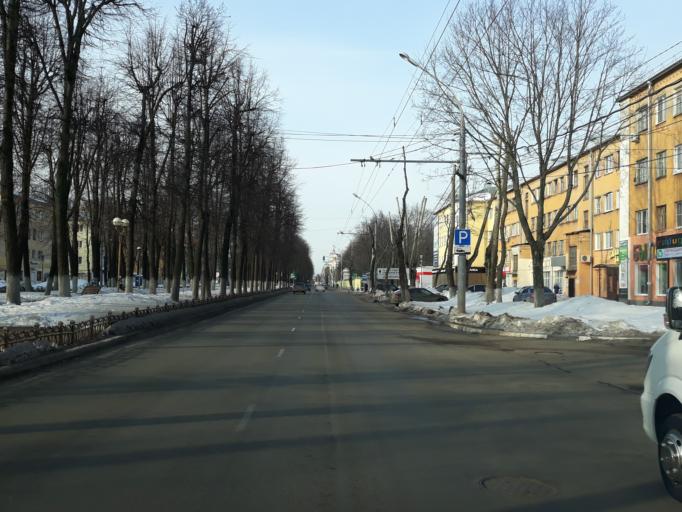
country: RU
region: Jaroslavl
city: Yaroslavl
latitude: 57.6395
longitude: 39.8734
